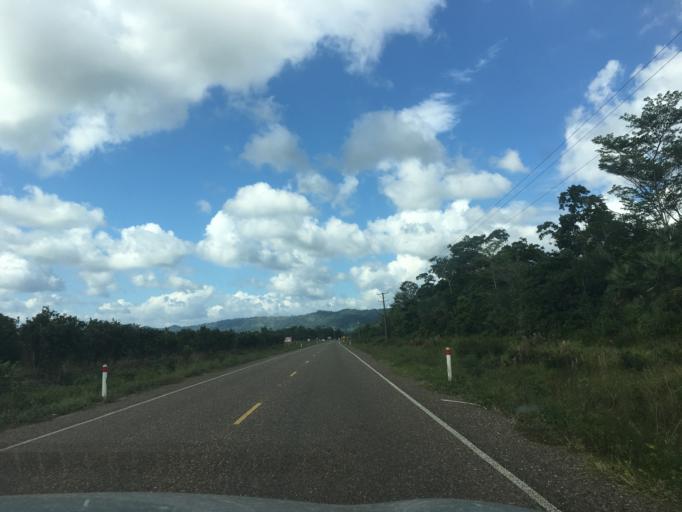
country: BZ
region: Stann Creek
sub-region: Dangriga
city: Dangriga
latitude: 16.8547
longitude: -88.3401
